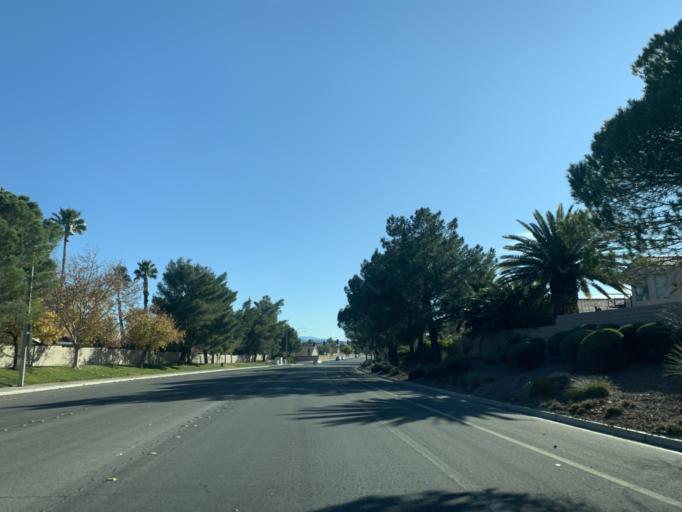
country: US
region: Nevada
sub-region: Clark County
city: Summerlin South
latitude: 36.1315
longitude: -115.3064
